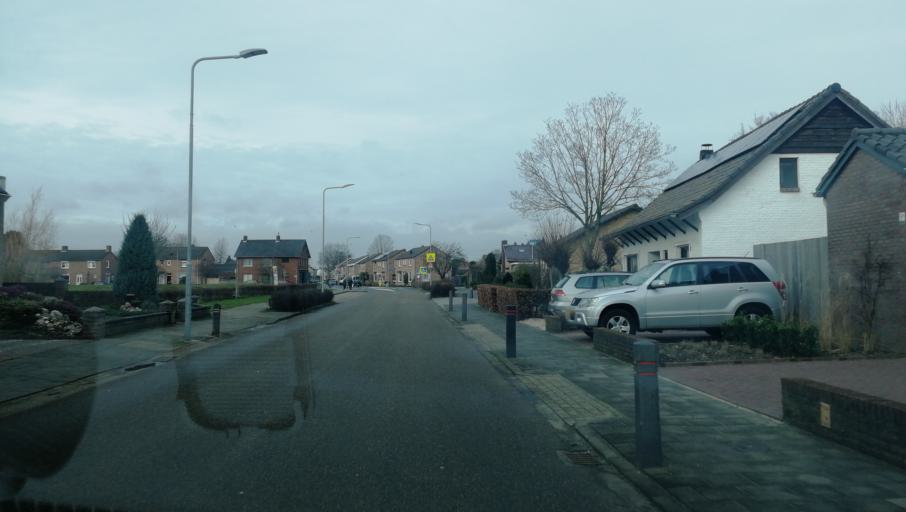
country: NL
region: Limburg
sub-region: Gemeente Beesel
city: Offenbeek
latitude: 51.3083
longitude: 6.1175
